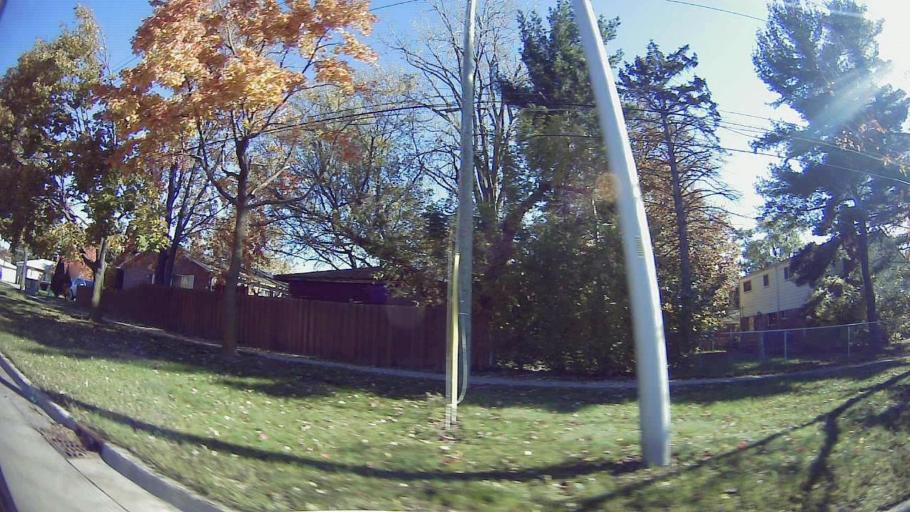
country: US
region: Michigan
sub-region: Oakland County
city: Farmington
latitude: 42.4445
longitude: -83.3754
